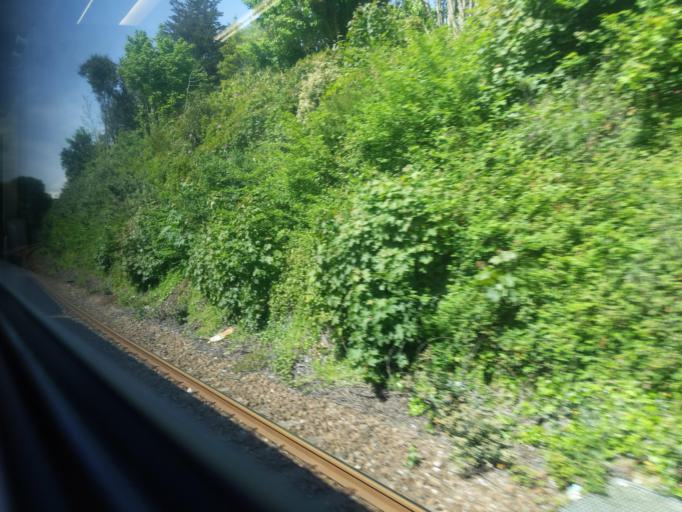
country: GB
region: England
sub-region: Cornwall
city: St Austell
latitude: 50.3405
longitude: -4.7936
